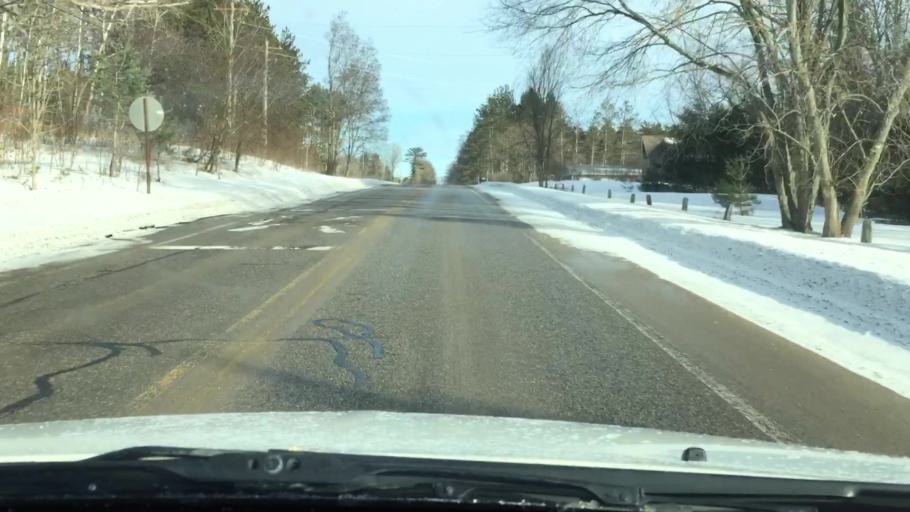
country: US
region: Michigan
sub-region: Kalkaska County
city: Kalkaska
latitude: 44.6413
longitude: -85.2771
